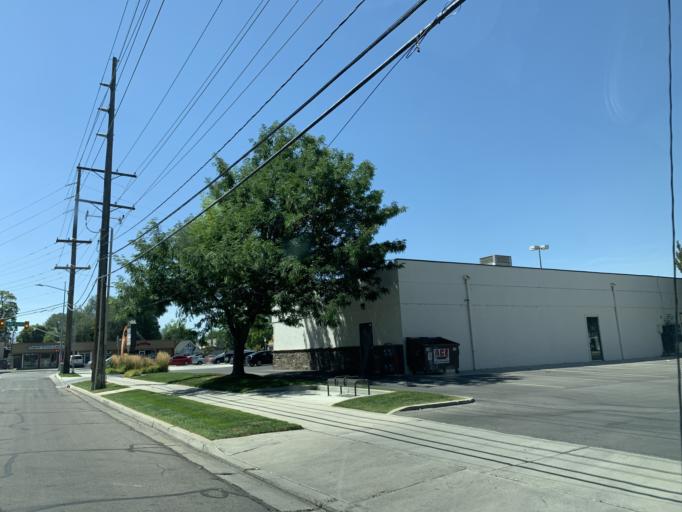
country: US
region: Utah
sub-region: Utah County
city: Provo
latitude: 40.2304
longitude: -111.6466
